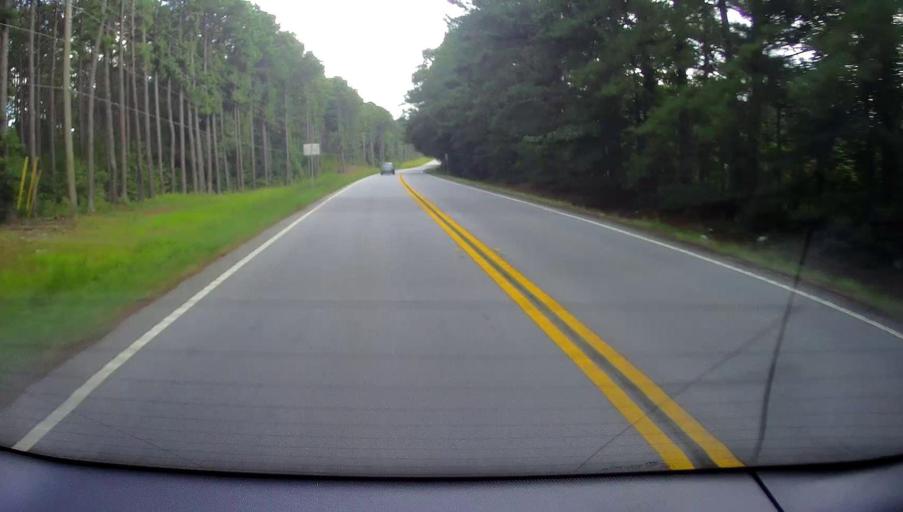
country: US
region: Georgia
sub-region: Meriwether County
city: Greenville
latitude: 33.0870
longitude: -84.5722
